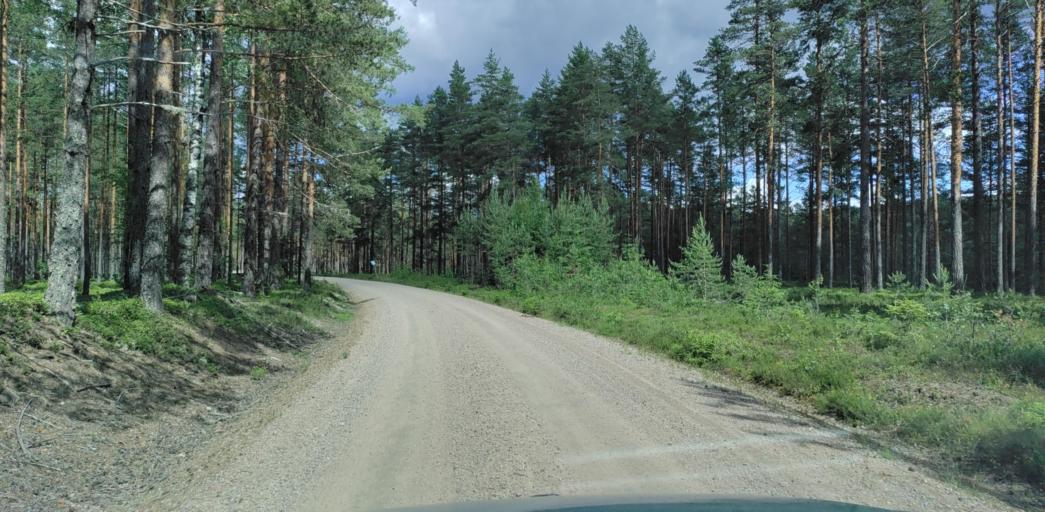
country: SE
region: Vaermland
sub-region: Hagfors Kommun
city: Ekshaerad
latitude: 60.0593
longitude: 13.2874
